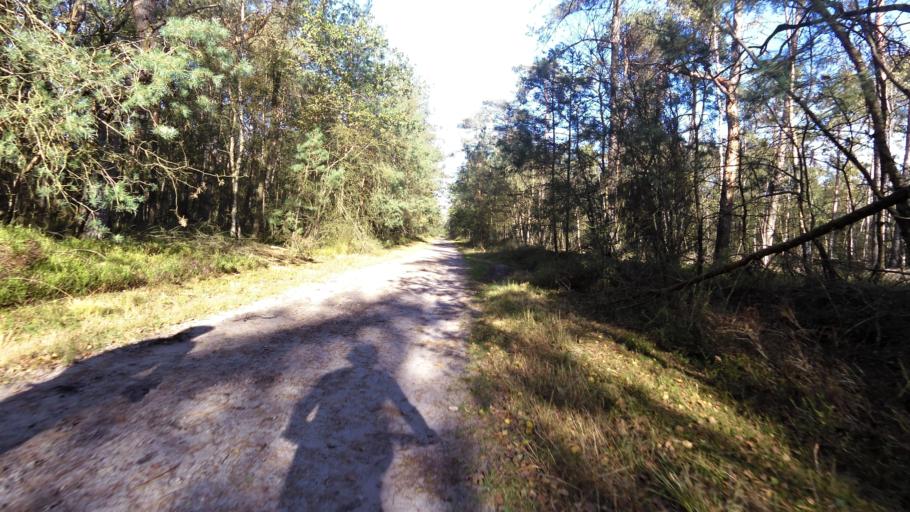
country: NL
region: Gelderland
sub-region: Gemeente Epe
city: Epe
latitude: 52.3718
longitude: 5.9452
